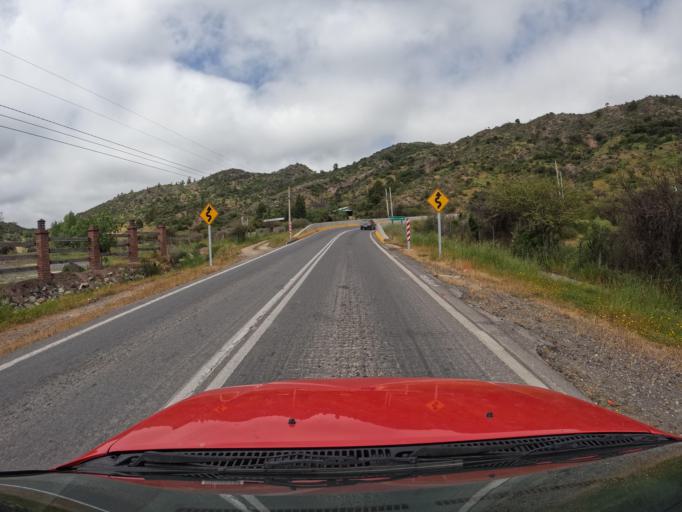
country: CL
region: O'Higgins
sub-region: Provincia de Colchagua
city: Santa Cruz
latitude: -34.6613
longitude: -71.4115
